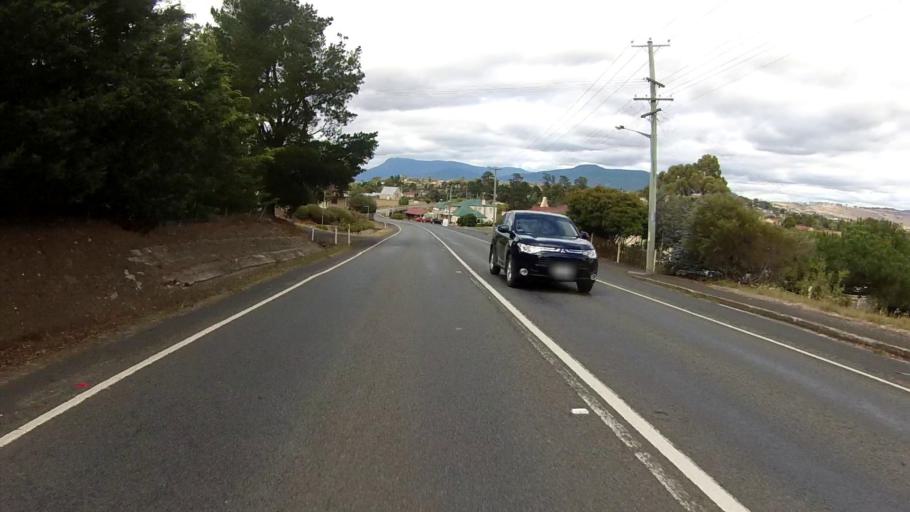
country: AU
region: Tasmania
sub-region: Brighton
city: Bridgewater
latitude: -42.6828
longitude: 147.2660
